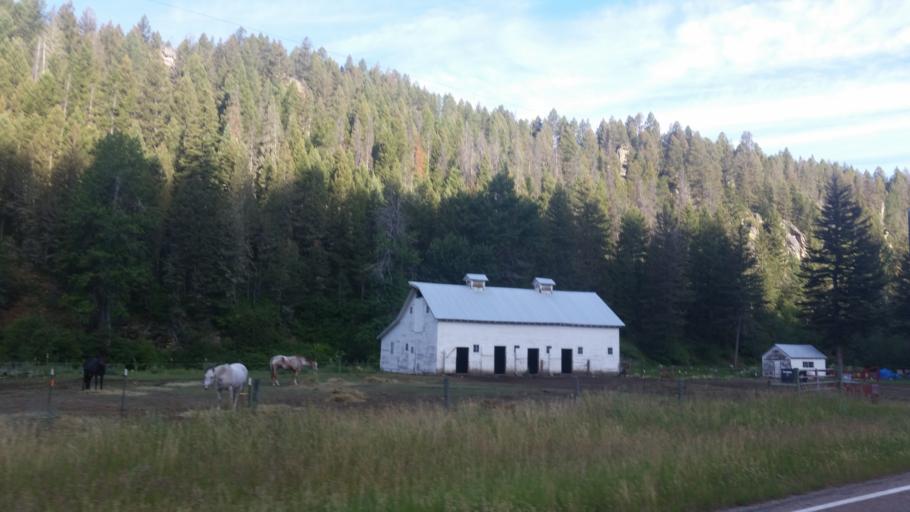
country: US
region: Montana
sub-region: Meagher County
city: White Sulphur Springs
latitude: 47.0461
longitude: -110.7931
